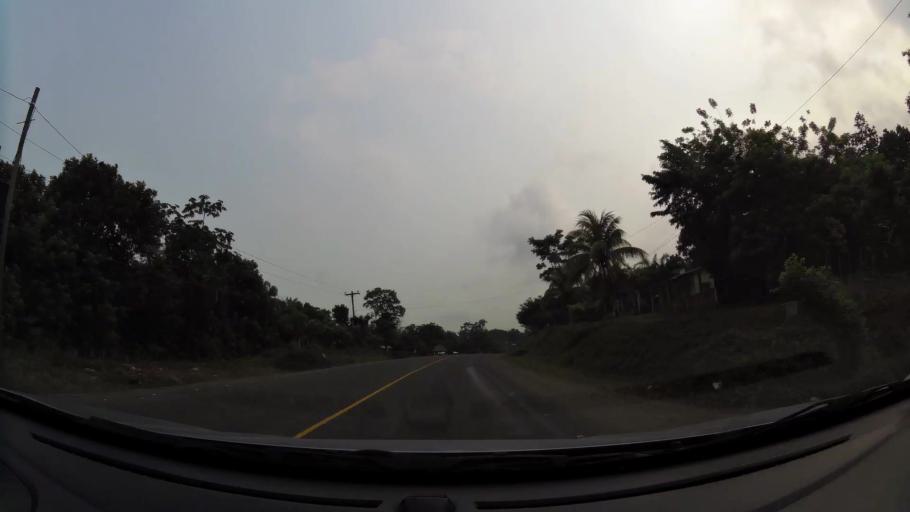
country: HN
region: Atlantida
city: Mezapa
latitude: 15.5707
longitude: -87.6184
